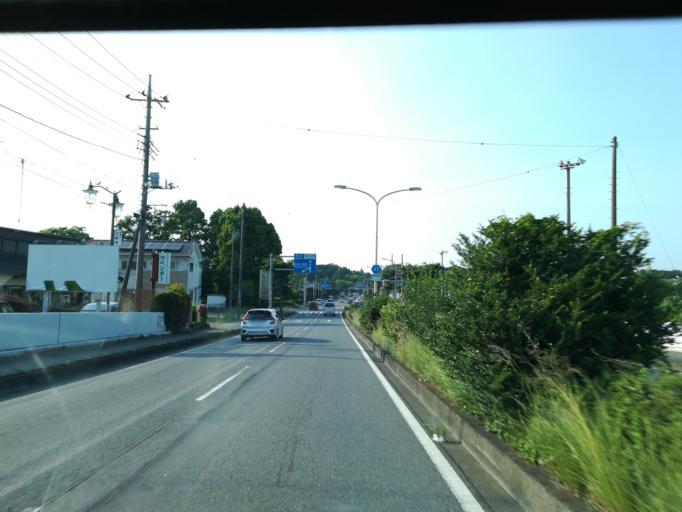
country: JP
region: Saitama
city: Kumagaya
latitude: 36.0470
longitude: 139.3765
